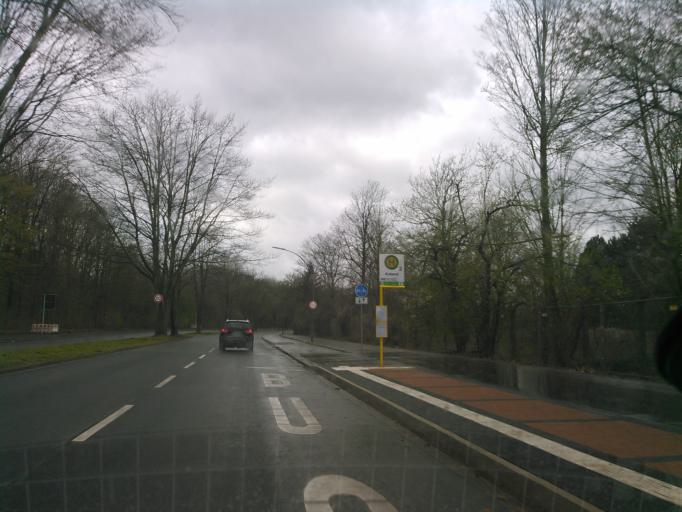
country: DE
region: North Rhine-Westphalia
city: Marl
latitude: 51.5960
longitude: 7.0651
